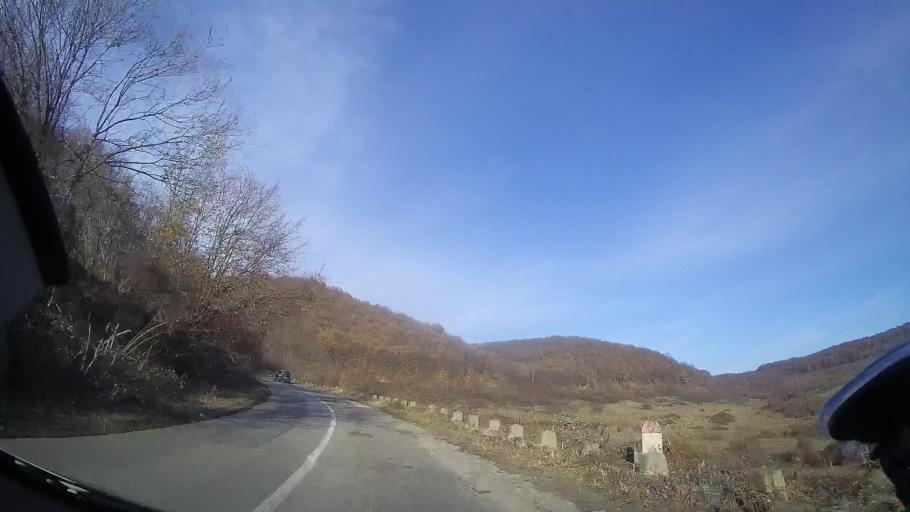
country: RO
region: Bihor
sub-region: Comuna Tileagd
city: Tileagd
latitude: 47.0930
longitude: 22.2360
